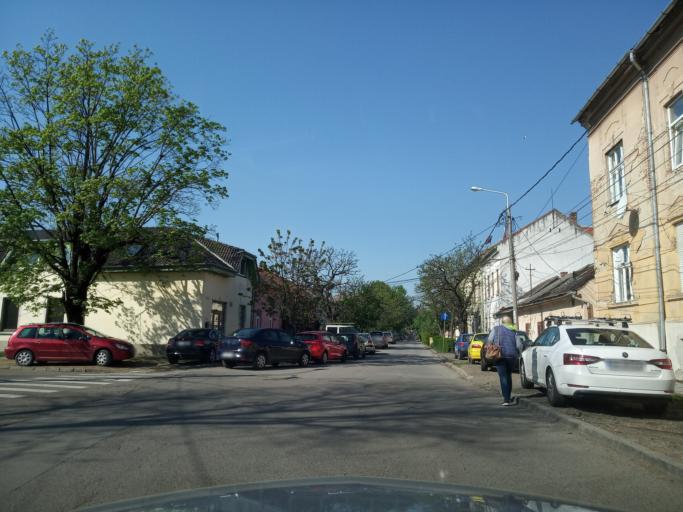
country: RO
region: Timis
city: Timisoara
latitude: 45.7405
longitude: 21.2318
